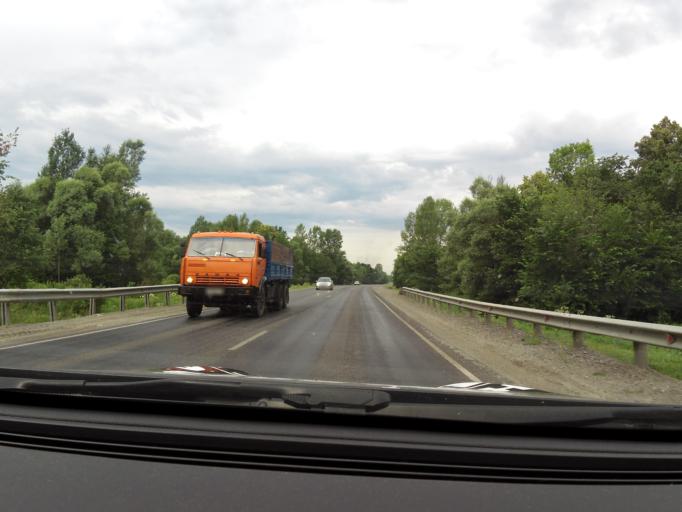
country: RU
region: Bashkortostan
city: Urman
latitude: 54.8279
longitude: 56.9186
